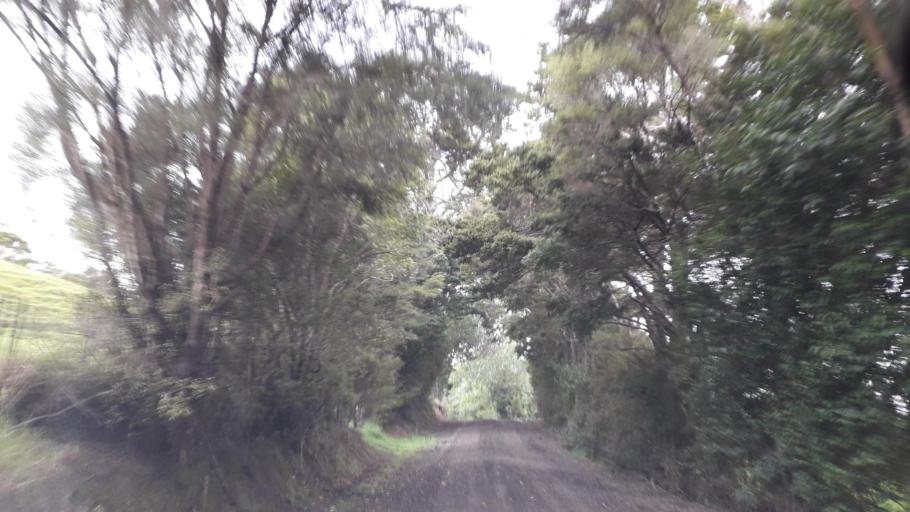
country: NZ
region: Northland
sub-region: Far North District
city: Waimate North
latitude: -35.3171
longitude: 173.5735
